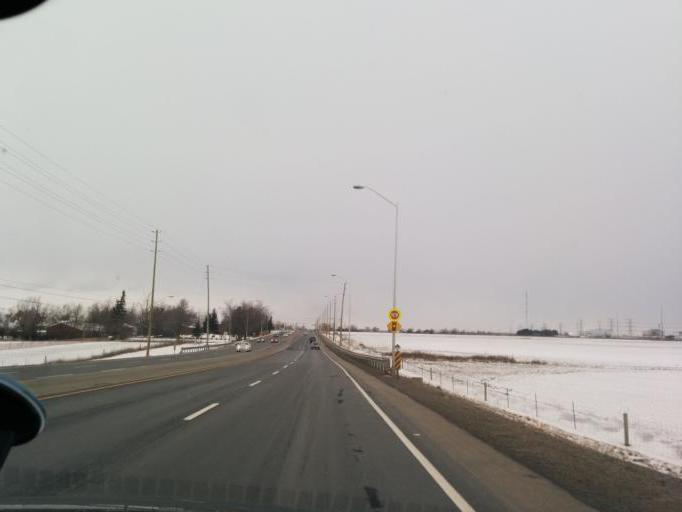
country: CA
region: Ontario
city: Brampton
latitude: 43.5951
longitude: -79.8118
